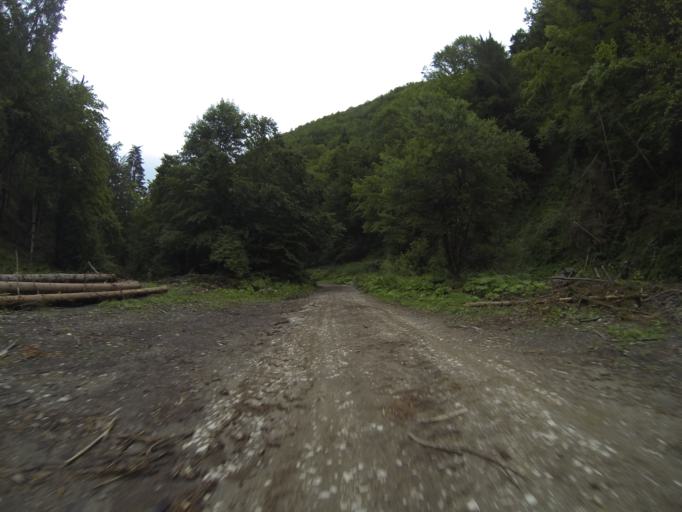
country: RO
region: Brasov
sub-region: Comuna Sinca Veche
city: Sinca Veche
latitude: 45.6863
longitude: 25.1465
